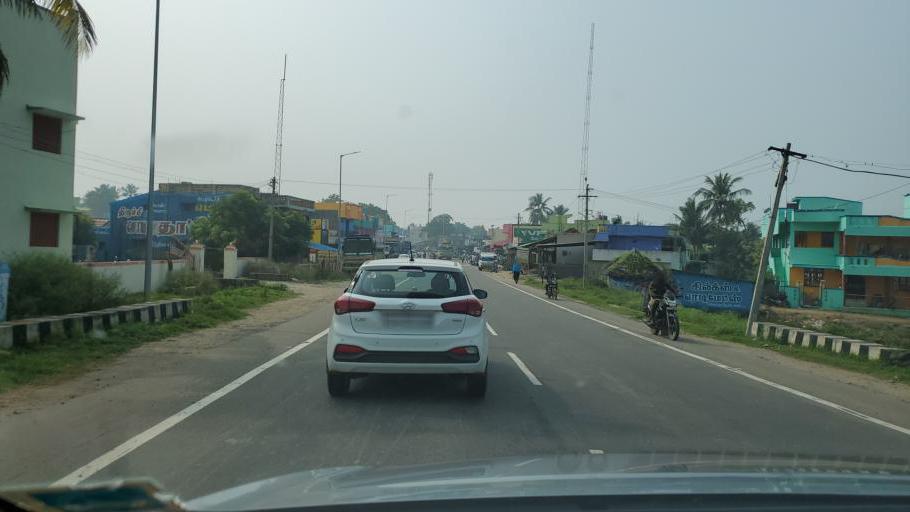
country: IN
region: Tamil Nadu
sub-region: Ariyalur
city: Ariyalur
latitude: 11.2360
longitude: 79.0219
